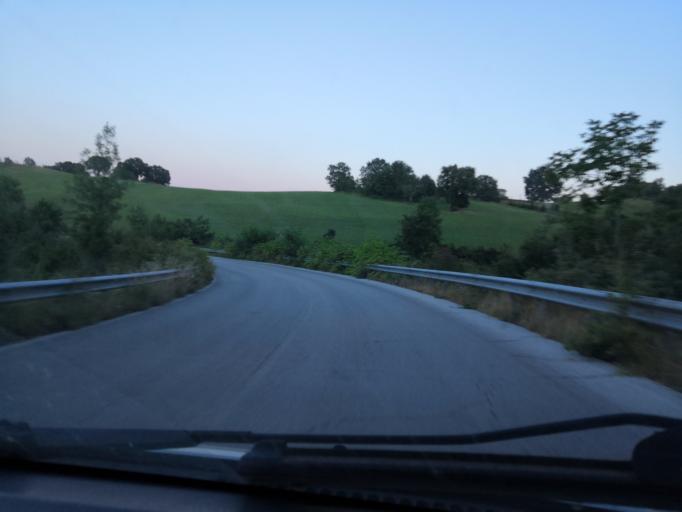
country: IT
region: Molise
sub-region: Provincia di Campobasso
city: Jelsi
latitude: 41.5099
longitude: 14.7750
